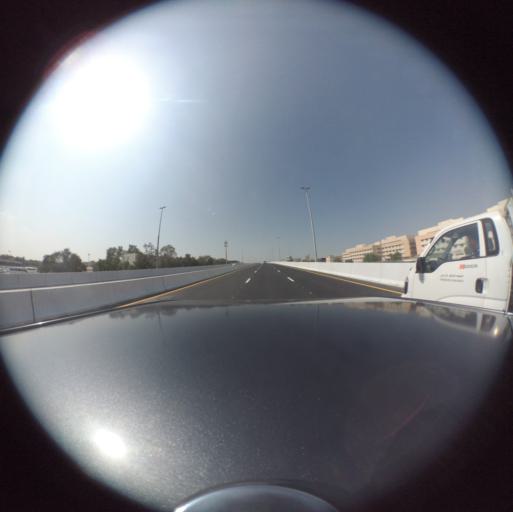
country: AE
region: Dubai
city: Dubai
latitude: 25.1498
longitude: 55.2457
